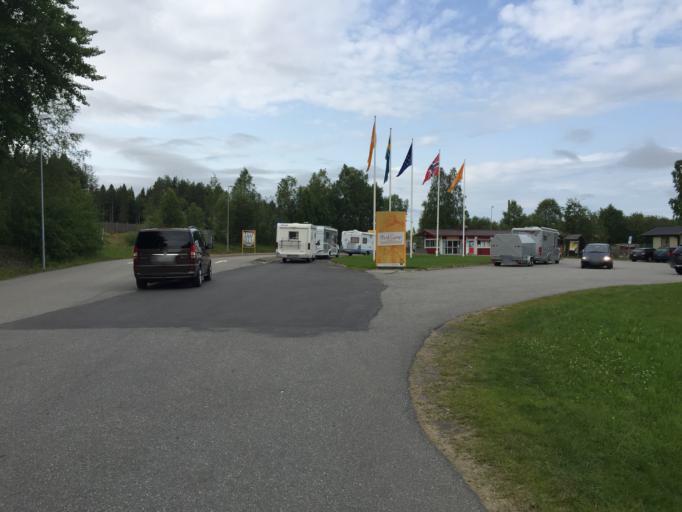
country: SE
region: Vaesterbotten
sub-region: Umea Kommun
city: Ersmark
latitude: 63.8425
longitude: 20.3401
